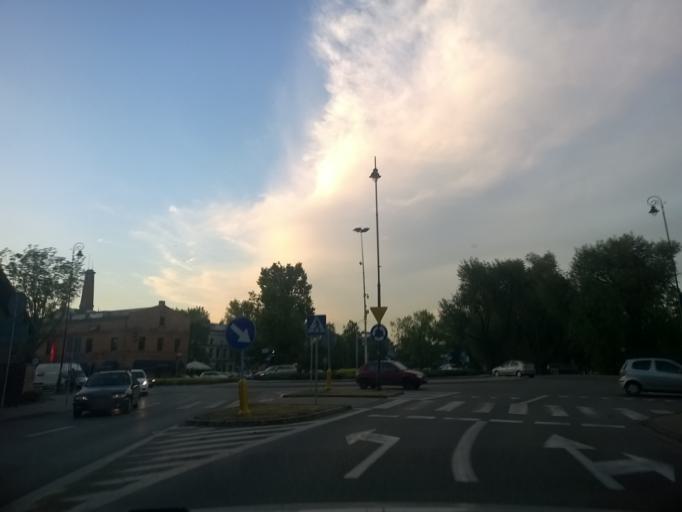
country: PL
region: Masovian Voivodeship
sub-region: Powiat piaseczynski
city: Konstancin-Jeziorna
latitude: 52.0899
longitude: 21.1218
